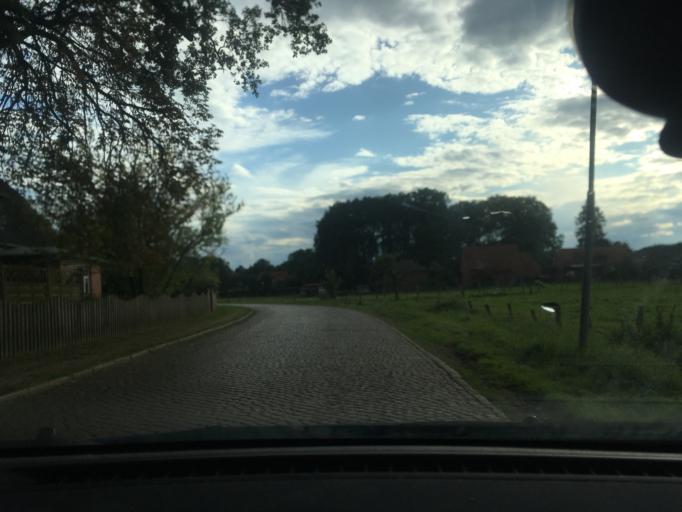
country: DE
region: Lower Saxony
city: Gohrde
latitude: 53.1659
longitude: 10.8675
